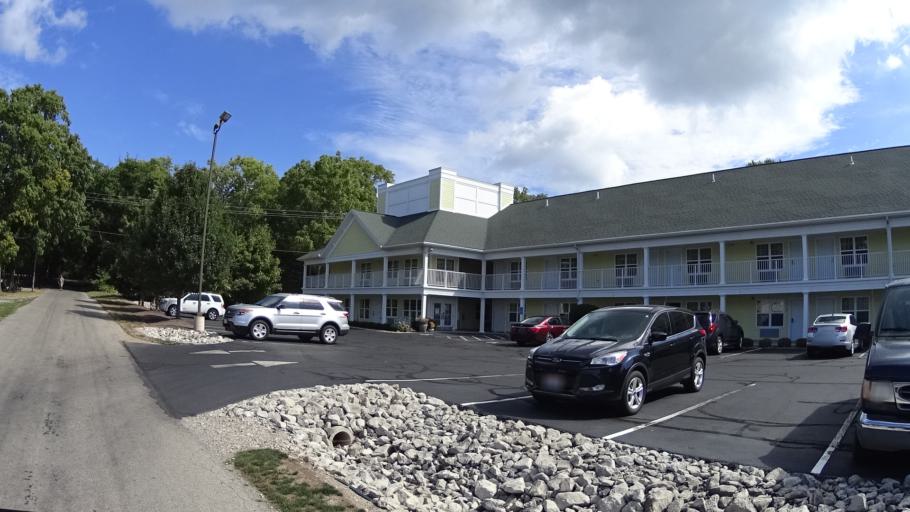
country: US
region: Ohio
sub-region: Erie County
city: Sandusky
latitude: 41.5964
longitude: -82.7251
